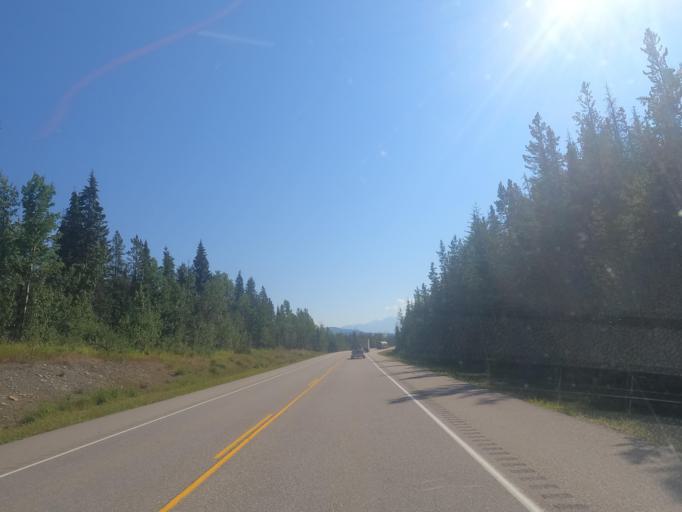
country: CA
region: Alberta
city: Jasper Park Lodge
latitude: 52.8764
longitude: -118.3199
